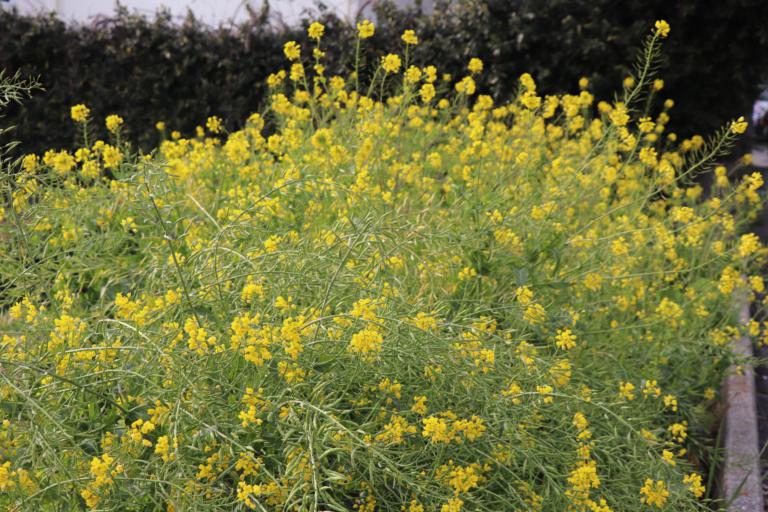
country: JP
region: Nagasaki
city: Shimabara
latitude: 32.6684
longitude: 130.3070
